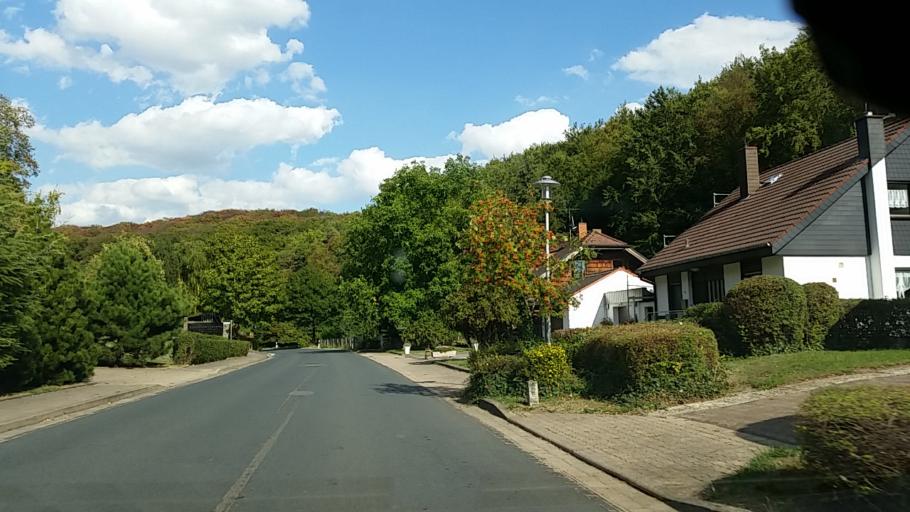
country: DE
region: Lower Saxony
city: Juhnde
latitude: 51.4281
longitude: 9.8387
